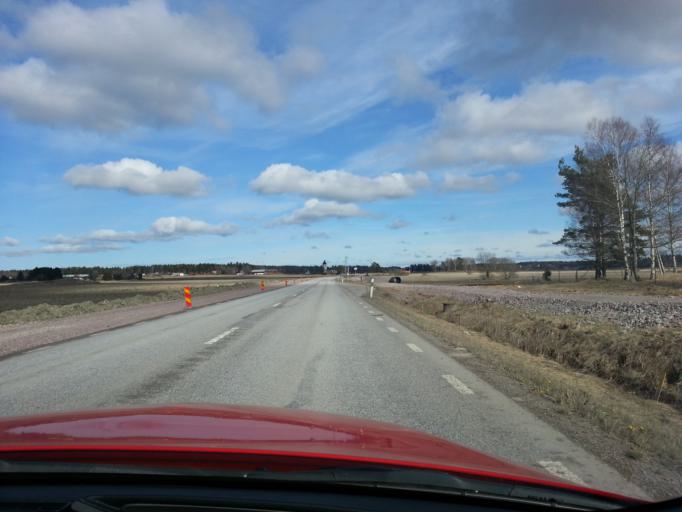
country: SE
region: Uppsala
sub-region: Osthammars Kommun
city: Gimo
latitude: 60.0505
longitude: 18.0523
